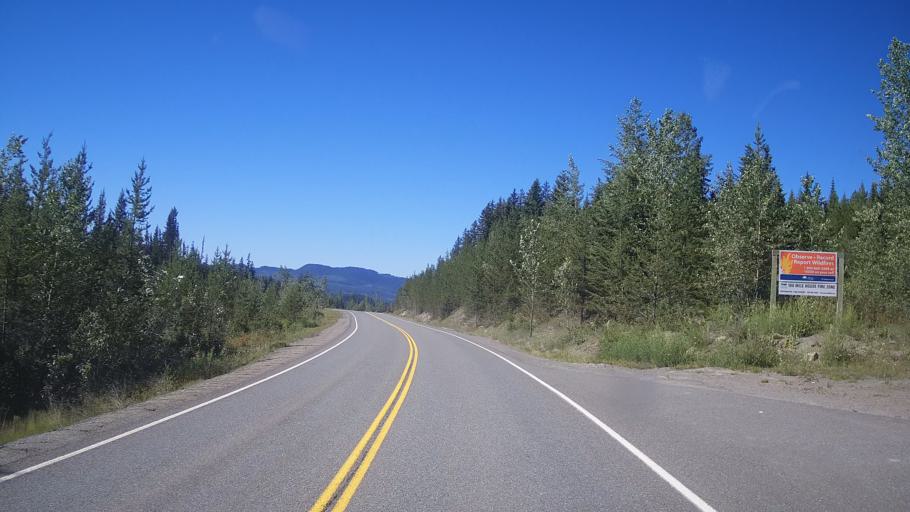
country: CA
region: British Columbia
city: Kamloops
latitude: 51.4964
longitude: -120.4510
